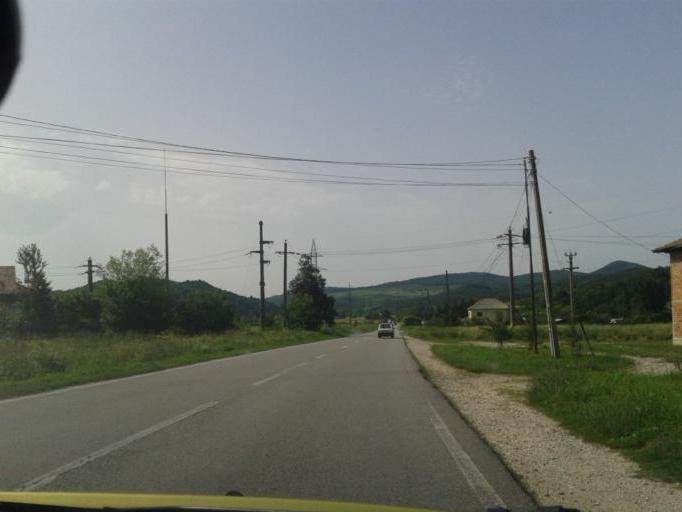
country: RO
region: Valcea
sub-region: Oras Baile Govora
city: Baile Govora
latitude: 45.0907
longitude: 24.2173
